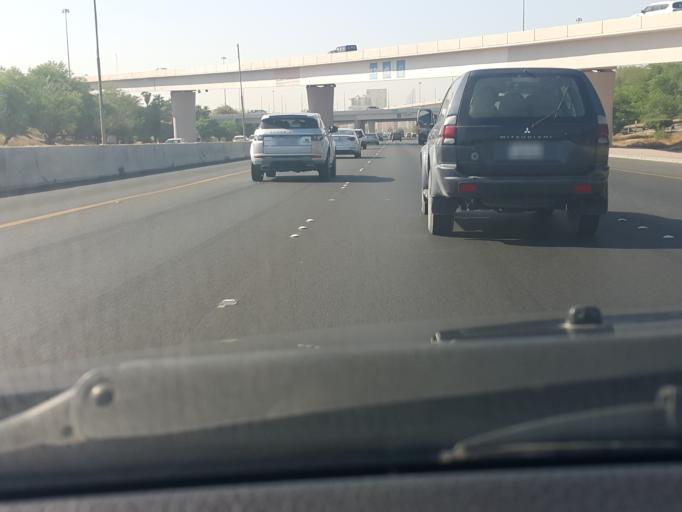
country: KW
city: Bayan
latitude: 29.3046
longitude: 48.0233
